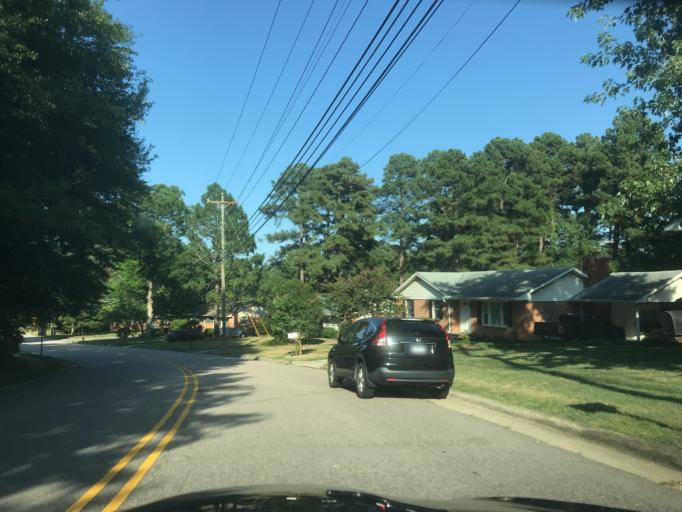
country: US
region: North Carolina
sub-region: Wake County
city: West Raleigh
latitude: 35.8421
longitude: -78.6387
